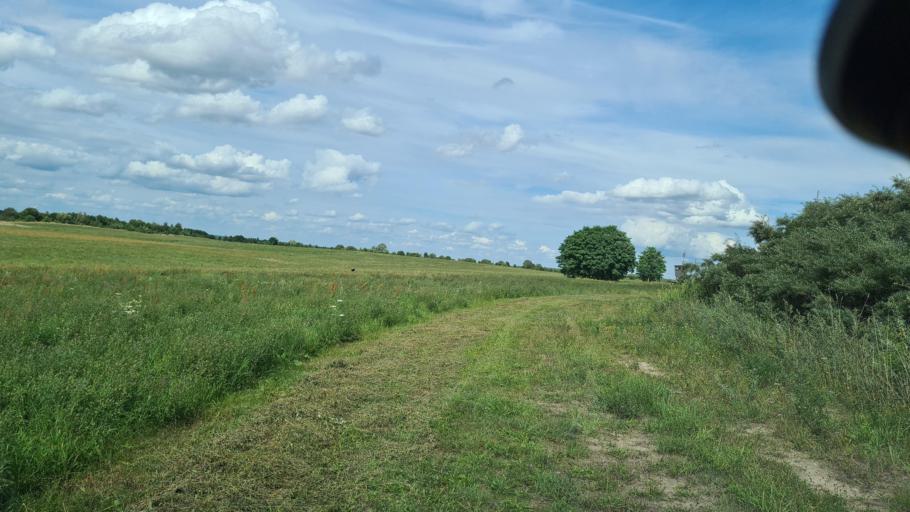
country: DE
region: Brandenburg
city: Spremberg
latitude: 51.5970
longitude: 14.3124
